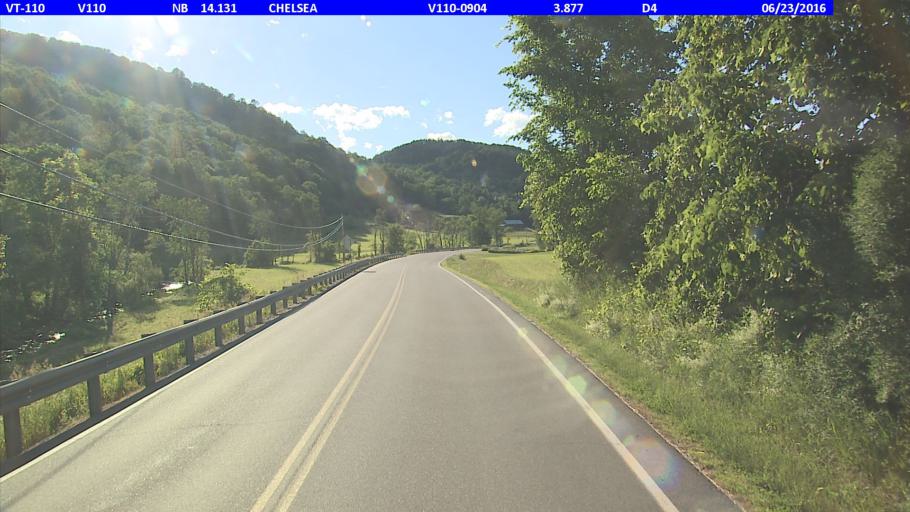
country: US
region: Vermont
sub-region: Orange County
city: Chelsea
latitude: 44.0004
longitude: -72.4531
